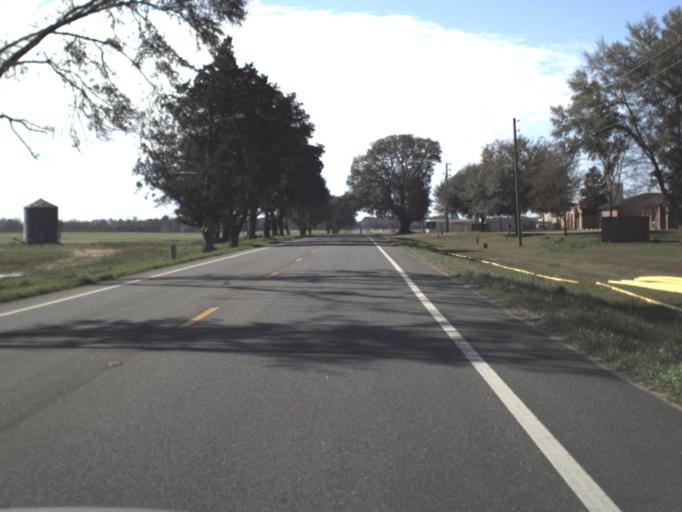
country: US
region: Florida
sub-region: Jackson County
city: Marianna
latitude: 30.8521
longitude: -85.1645
